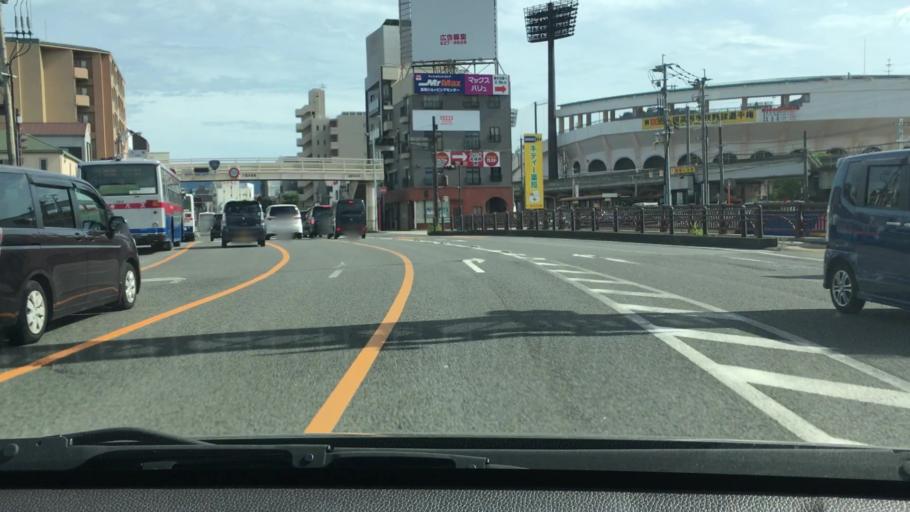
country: JP
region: Nagasaki
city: Nagasaki-shi
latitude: 32.7789
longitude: 129.8618
